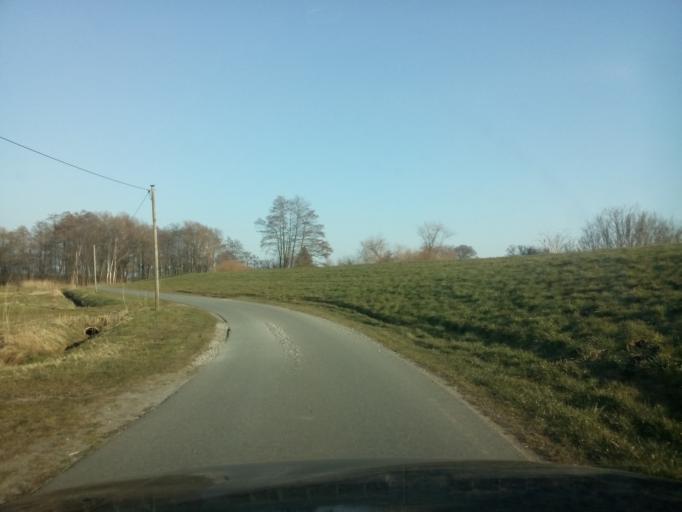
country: DE
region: Lower Saxony
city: Osterholz-Scharmbeck
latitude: 53.1584
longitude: 8.8371
